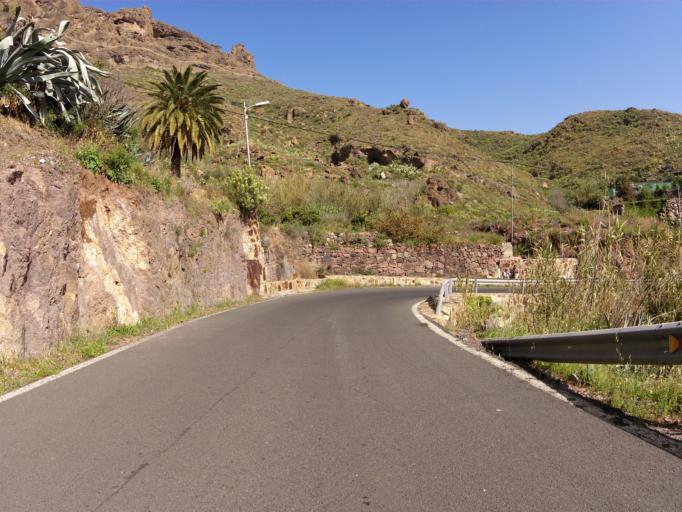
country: ES
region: Canary Islands
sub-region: Provincia de Las Palmas
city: Mogan
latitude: 27.9066
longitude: -15.6714
